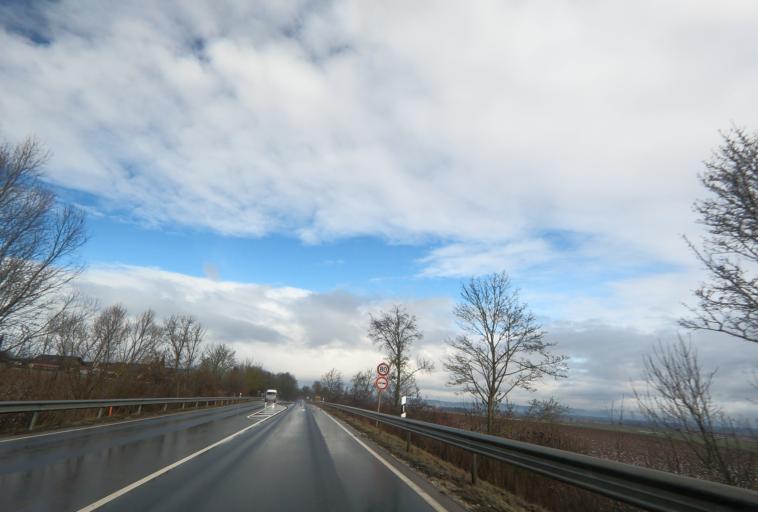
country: DE
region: Bavaria
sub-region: Upper Palatinate
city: Alteglofsheim
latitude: 48.9116
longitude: 12.2099
